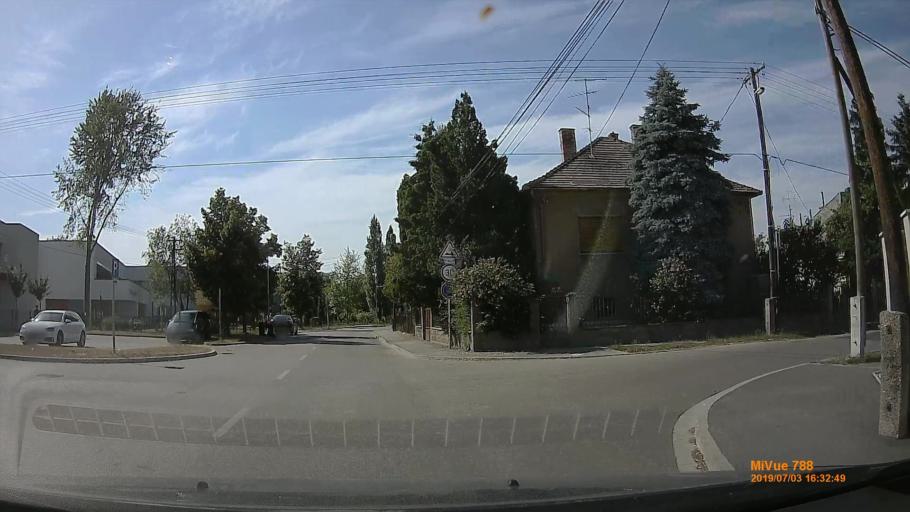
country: HU
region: Gyor-Moson-Sopron
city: Gyor
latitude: 47.7026
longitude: 17.6380
